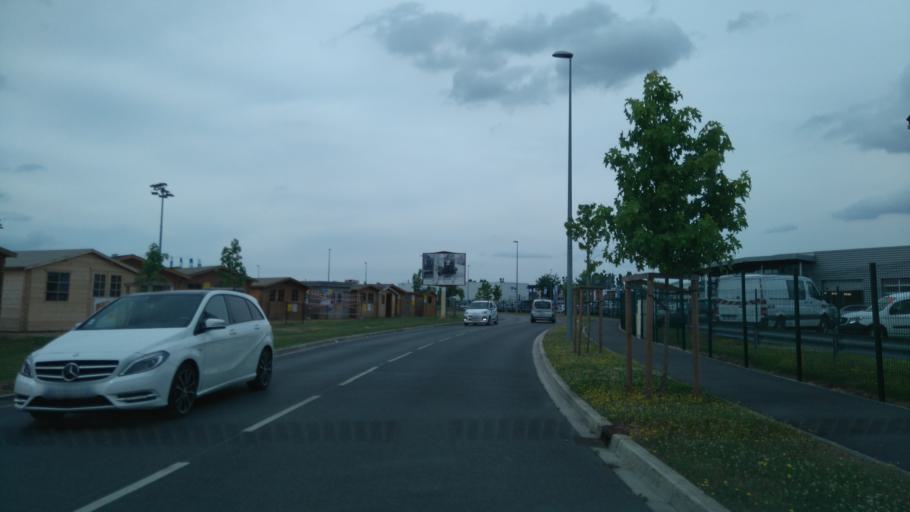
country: FR
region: Picardie
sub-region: Departement de l'Oise
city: Saint-Maximin
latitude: 49.2299
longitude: 2.4665
